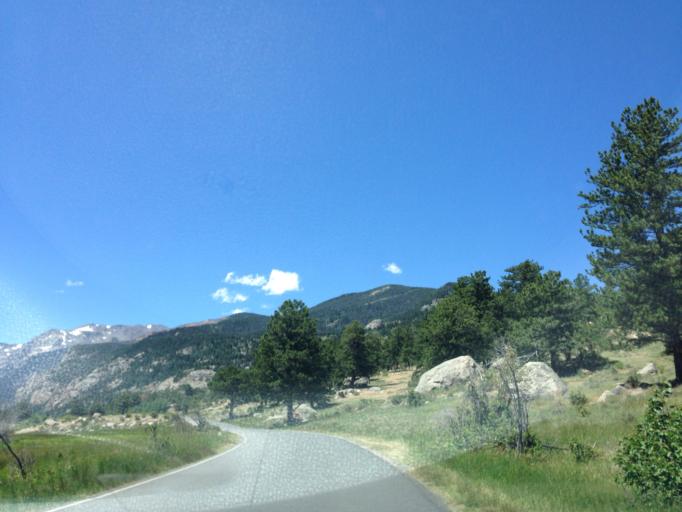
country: US
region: Colorado
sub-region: Larimer County
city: Estes Park
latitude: 40.3569
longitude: -105.6059
